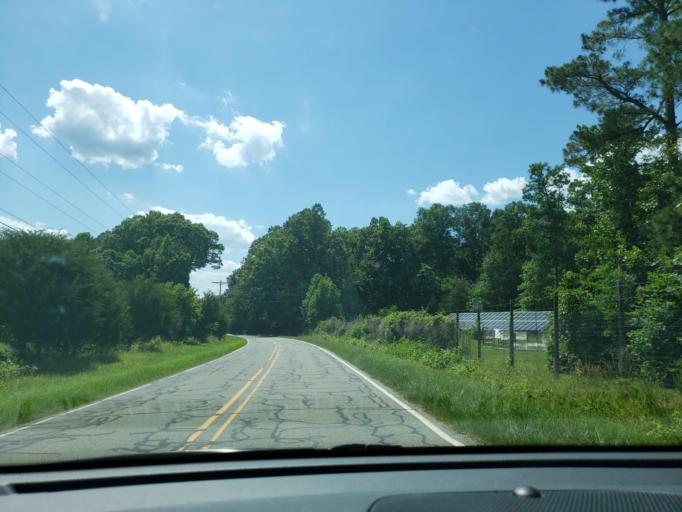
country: US
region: North Carolina
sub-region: Orange County
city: Chapel Hill
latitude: 36.0022
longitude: -79.0297
